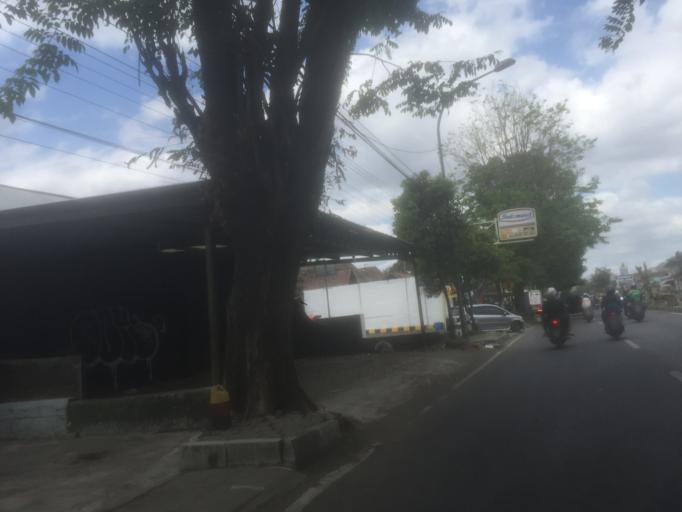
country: ID
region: Daerah Istimewa Yogyakarta
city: Melati
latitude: -7.7305
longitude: 110.3635
